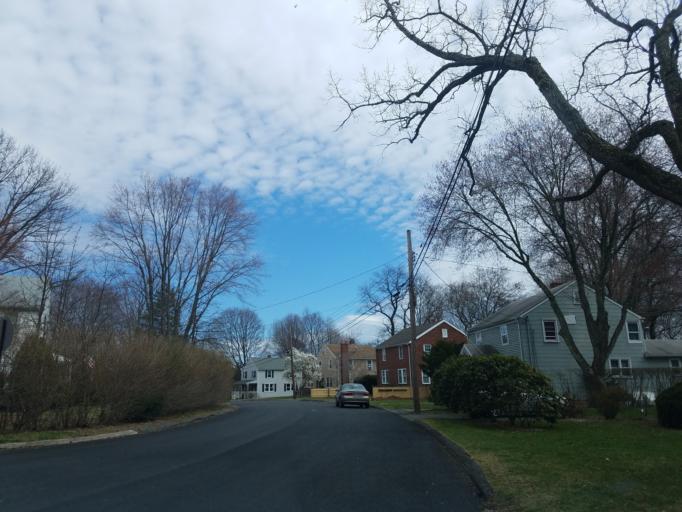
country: US
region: Connecticut
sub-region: Fairfield County
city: Bridgeport
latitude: 41.1894
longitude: -73.2398
